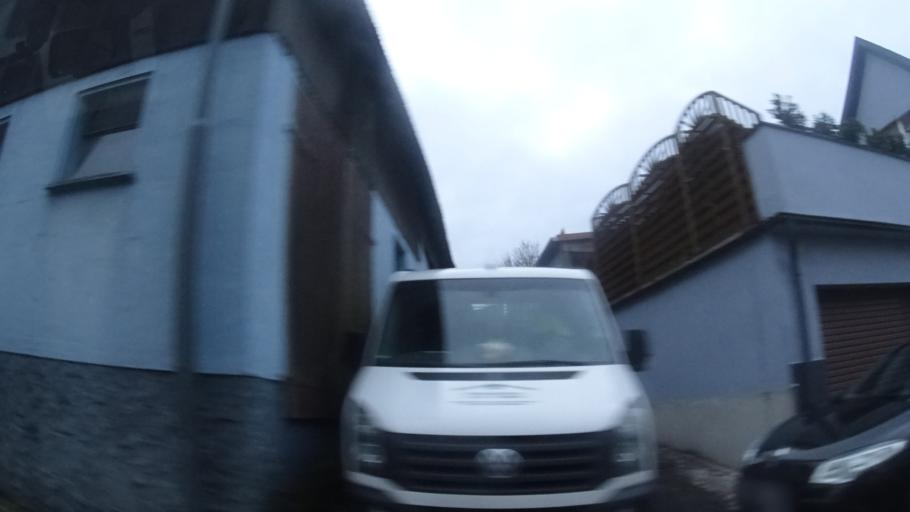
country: DE
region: Hesse
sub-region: Regierungsbezirk Giessen
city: Freiensteinau
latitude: 50.3682
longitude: 9.4225
